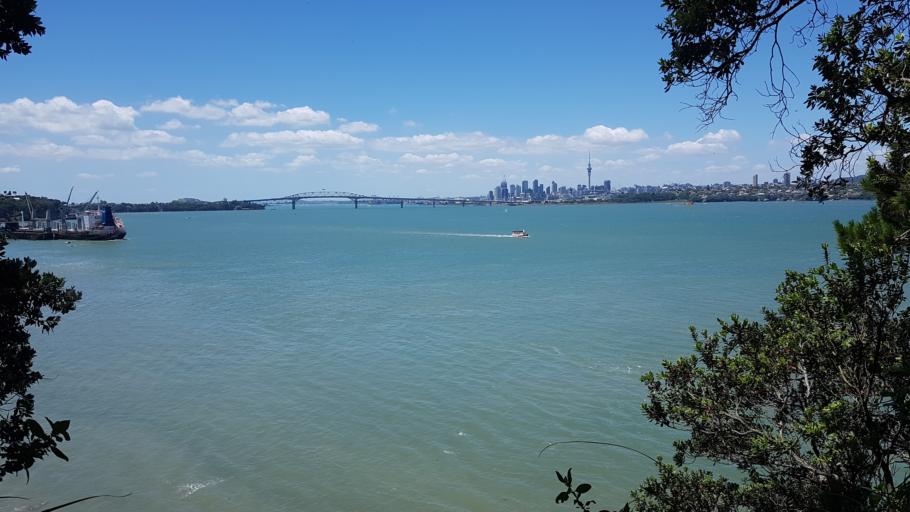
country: NZ
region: Auckland
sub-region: Auckland
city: North Shore
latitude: -36.8240
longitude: 174.7159
